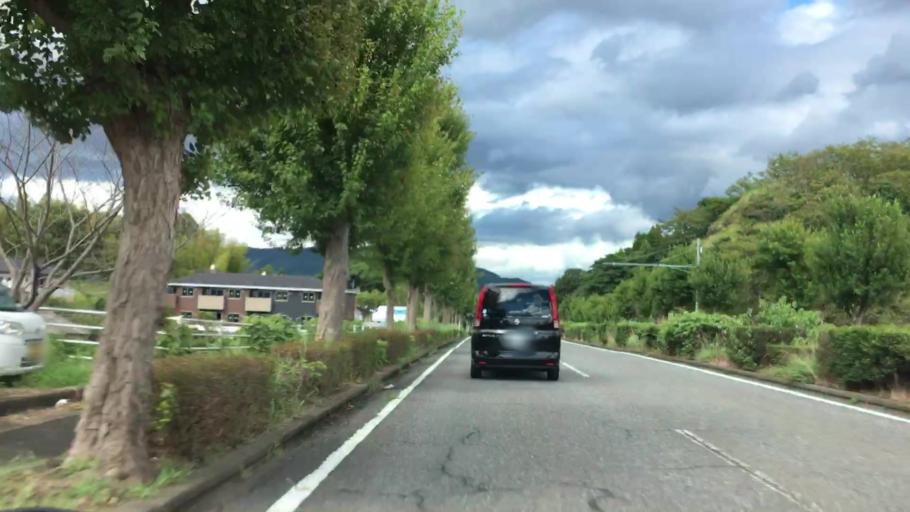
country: JP
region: Saga Prefecture
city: Imaricho-ko
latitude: 33.2662
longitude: 129.8654
